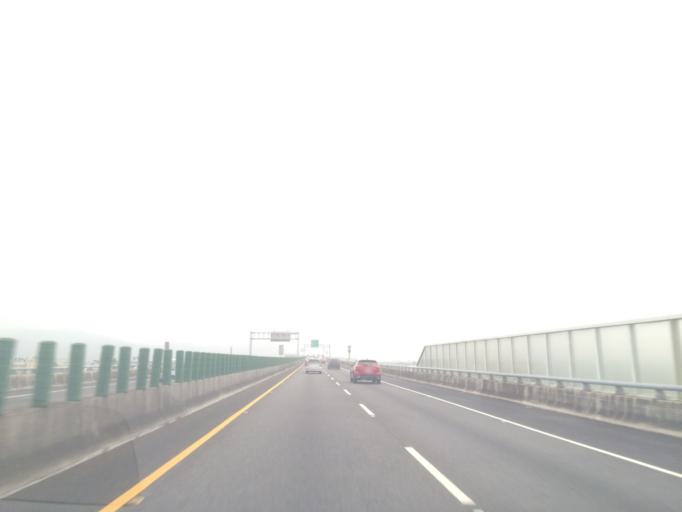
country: TW
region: Taiwan
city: Zhongxing New Village
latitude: 24.0242
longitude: 120.6748
